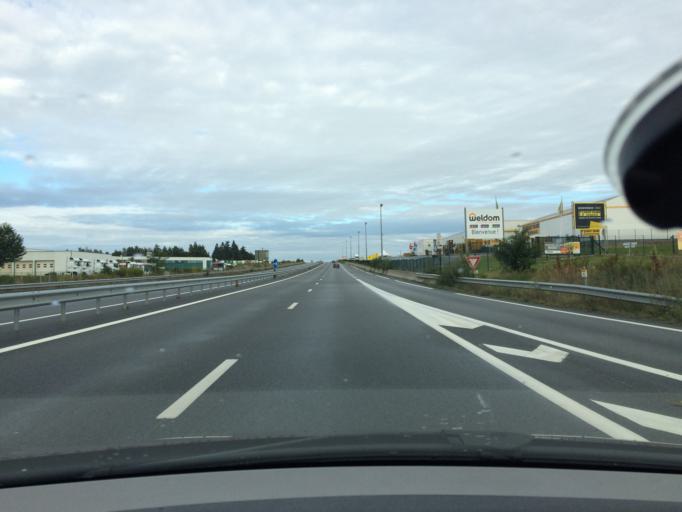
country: FR
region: Brittany
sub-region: Departement d'Ille-et-Vilaine
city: Janze
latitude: 47.9719
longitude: -1.5389
